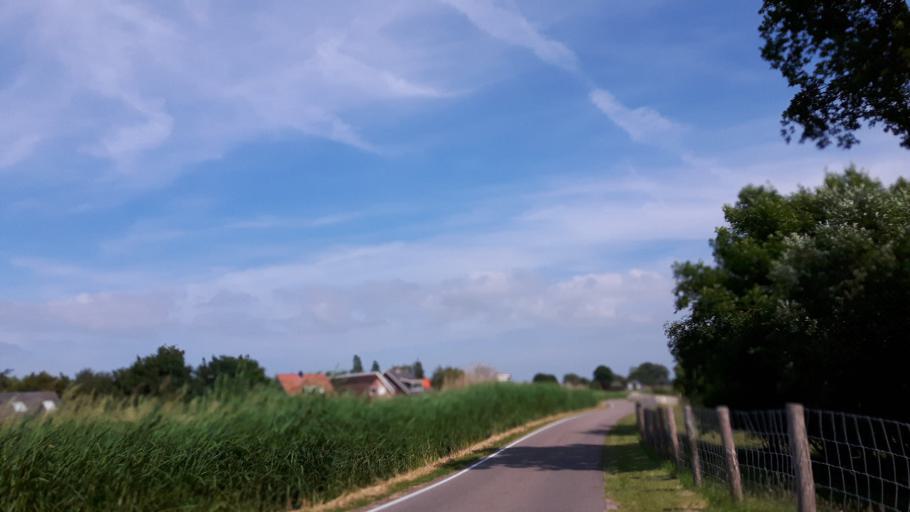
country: NL
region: North Holland
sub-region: Gemeente Uithoorn
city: Uithoorn
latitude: 52.1989
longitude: 4.8146
